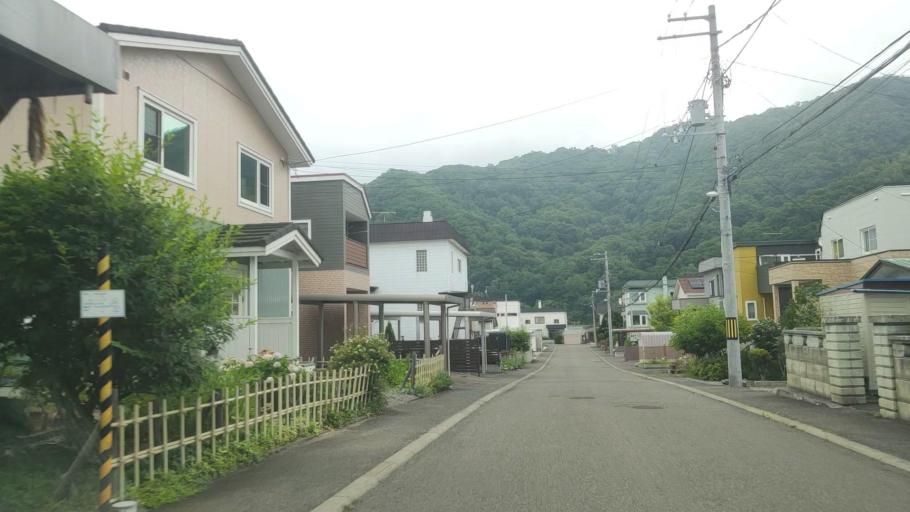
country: JP
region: Hokkaido
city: Sapporo
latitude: 42.9632
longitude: 141.3174
